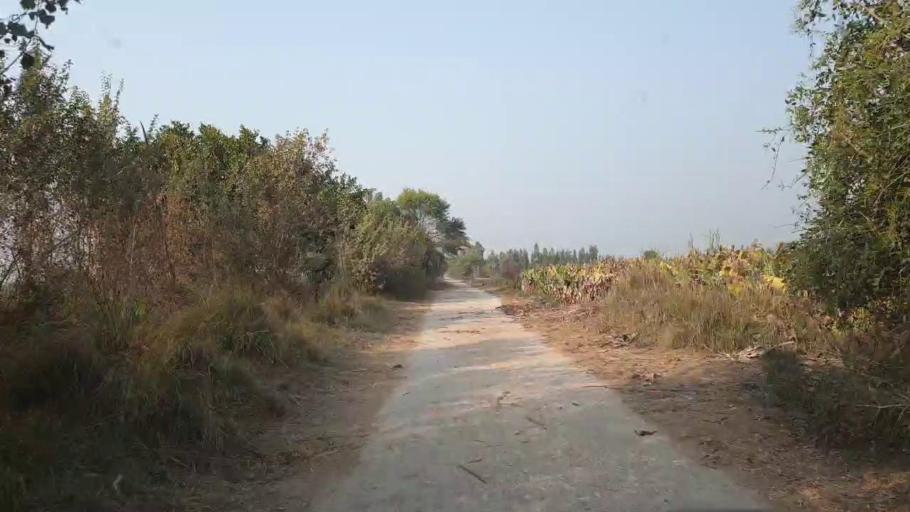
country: PK
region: Sindh
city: Hala
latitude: 25.9081
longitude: 68.4618
